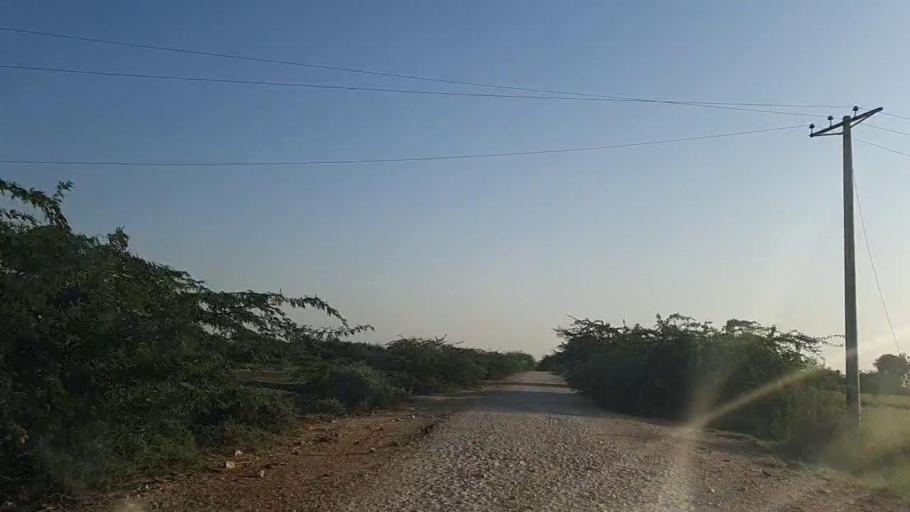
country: PK
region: Sindh
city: Jati
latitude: 24.4177
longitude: 68.1853
